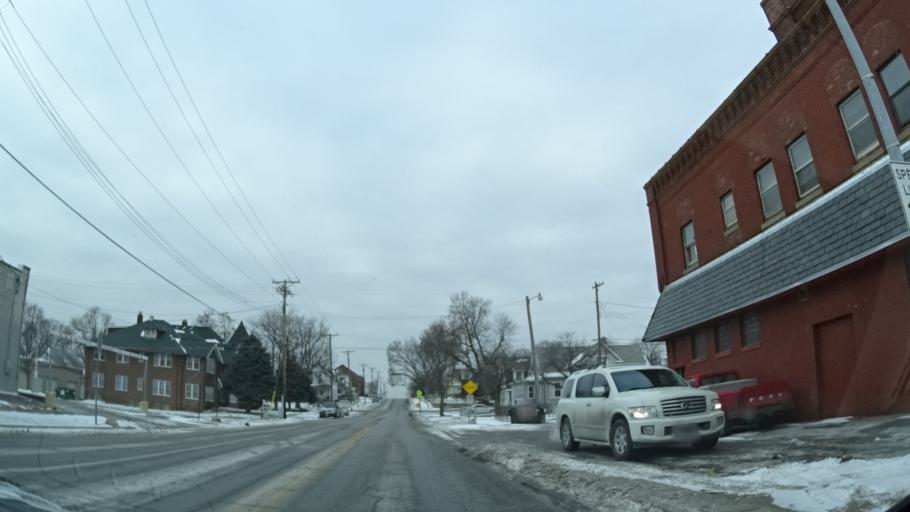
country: US
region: Nebraska
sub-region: Douglas County
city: Omaha
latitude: 41.2197
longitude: -95.9473
